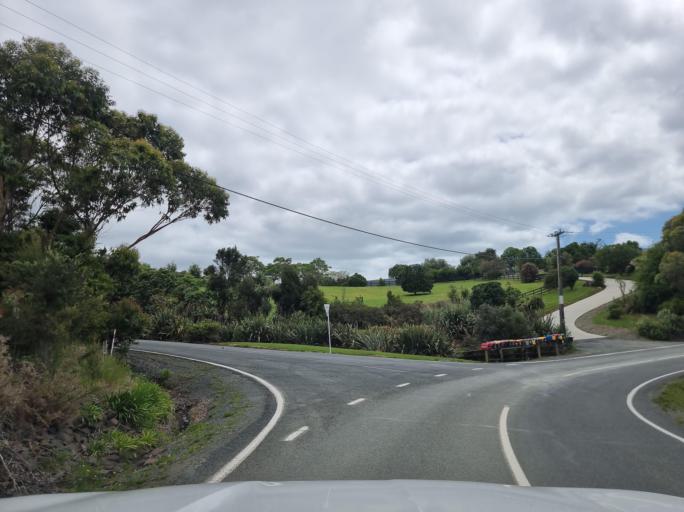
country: NZ
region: Auckland
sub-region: Auckland
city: Wellsford
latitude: -36.0904
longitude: 174.5300
